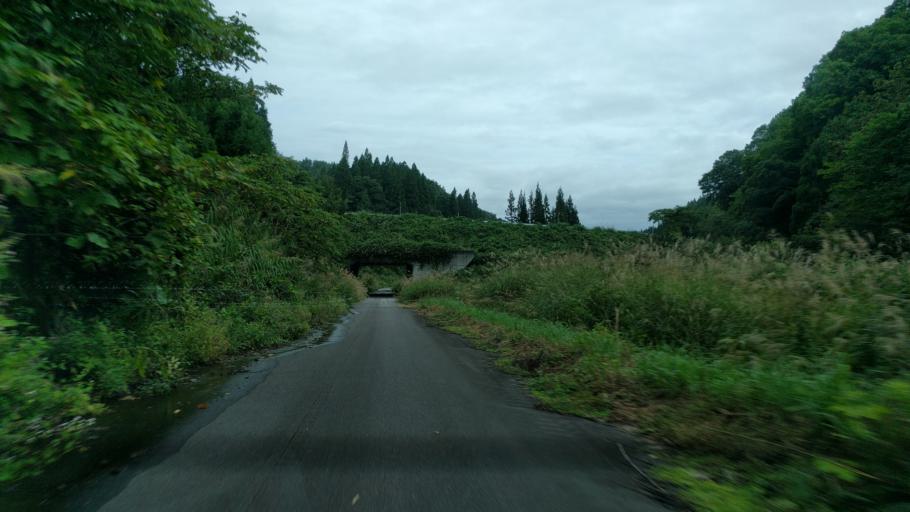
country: JP
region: Fukushima
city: Kitakata
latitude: 37.4698
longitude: 139.7727
